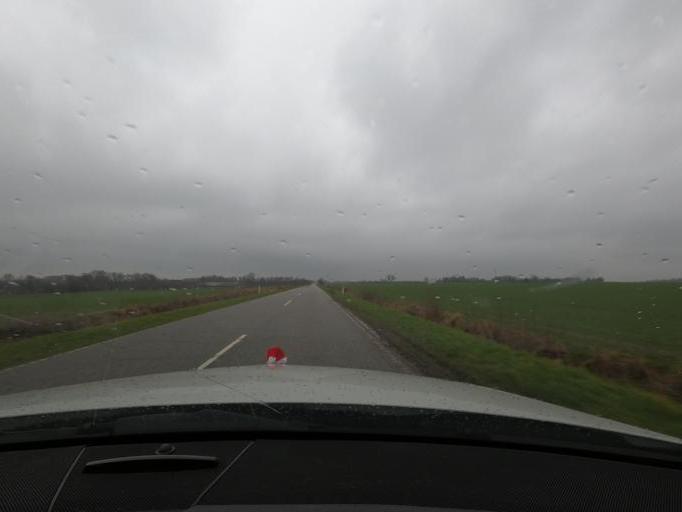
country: DK
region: South Denmark
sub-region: Haderslev Kommune
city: Starup
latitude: 55.2372
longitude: 9.6501
